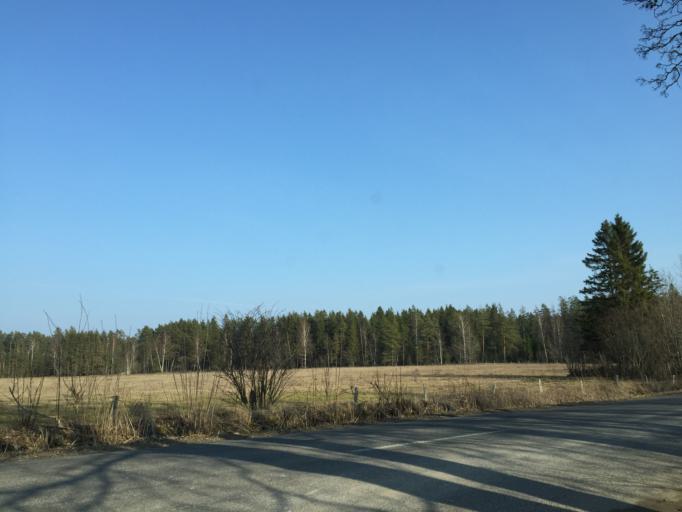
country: EE
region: Saare
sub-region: Orissaare vald
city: Orissaare
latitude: 58.6067
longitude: 23.3113
